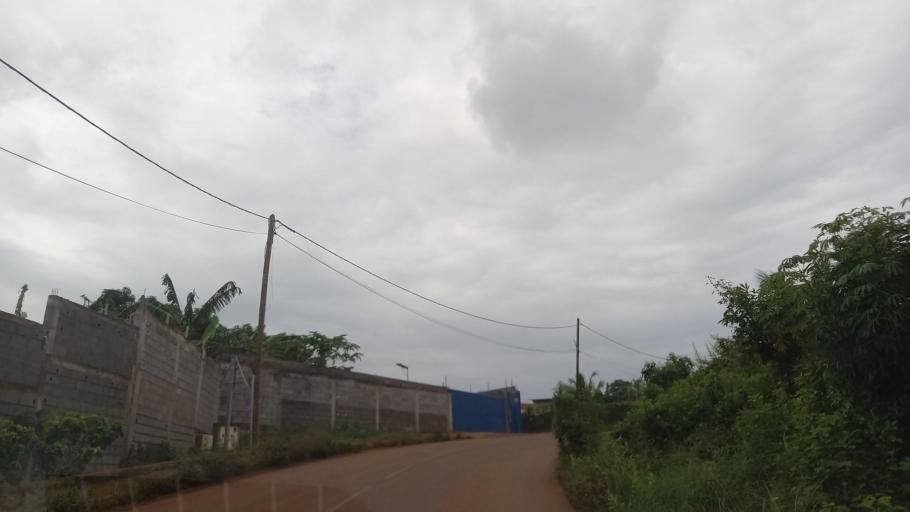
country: YT
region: Chiconi
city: Chiconi
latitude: -12.8283
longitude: 45.1283
